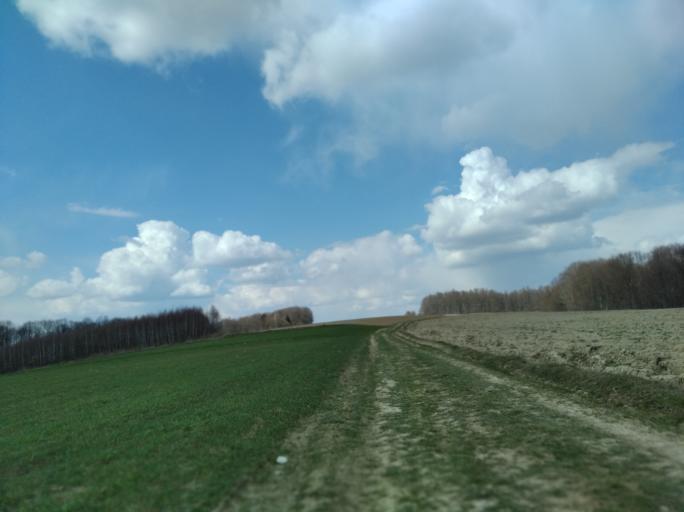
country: PL
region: Subcarpathian Voivodeship
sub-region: Powiat strzyzowski
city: Strzyzow
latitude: 49.9170
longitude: 21.7450
